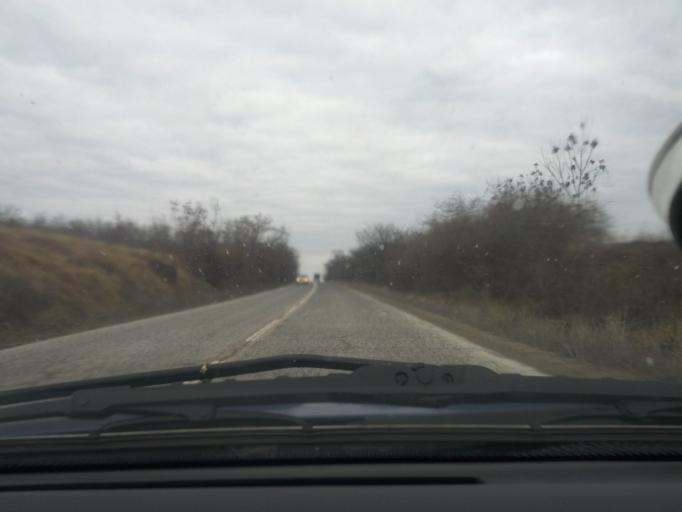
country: BG
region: Vratsa
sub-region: Obshtina Vratsa
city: Vratsa
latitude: 43.3051
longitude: 23.6690
